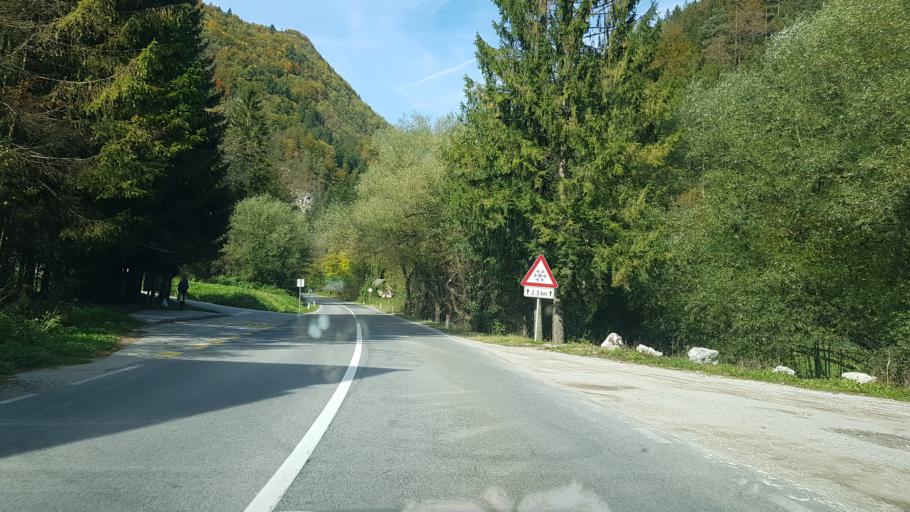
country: SI
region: Velenje
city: Velenje
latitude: 46.4113
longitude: 15.1779
